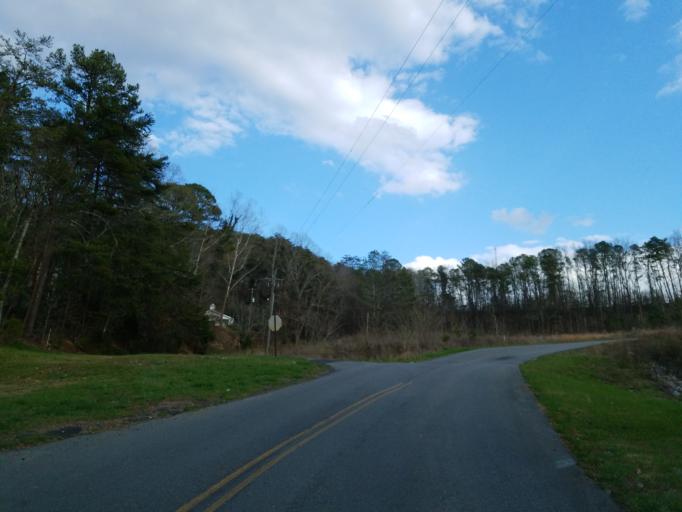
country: US
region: Georgia
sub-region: Bartow County
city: Rydal
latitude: 34.4344
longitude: -84.6937
